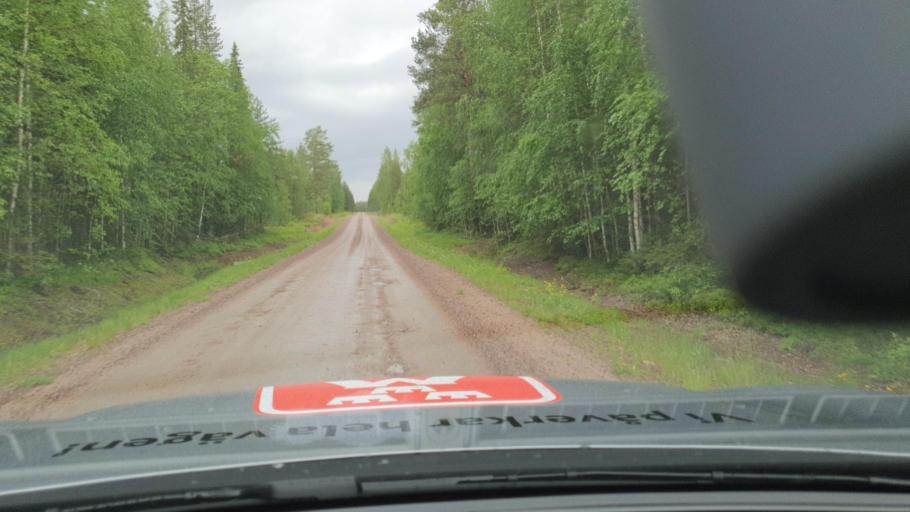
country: SE
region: Norrbotten
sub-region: Overkalix Kommun
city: OEverkalix
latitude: 66.6163
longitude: 22.7312
